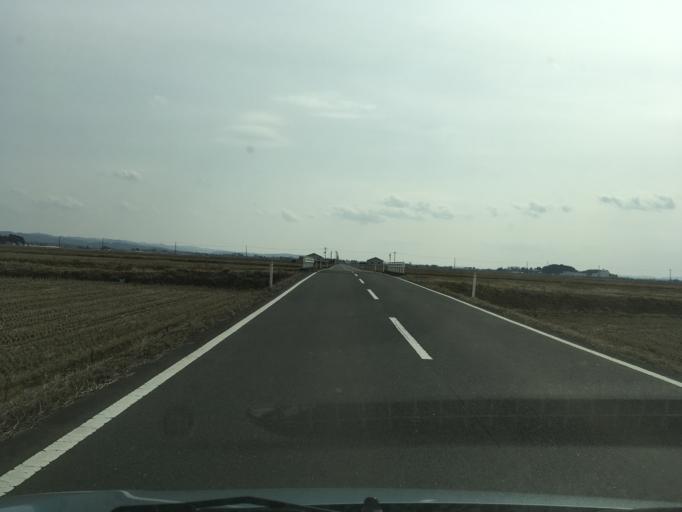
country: JP
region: Iwate
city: Ichinoseki
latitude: 38.7495
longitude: 141.2370
